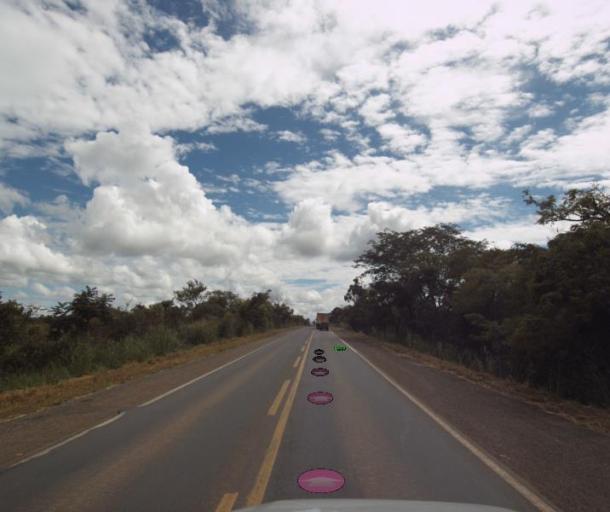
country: BR
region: Goias
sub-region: Uruacu
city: Uruacu
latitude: -14.4513
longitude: -49.1564
